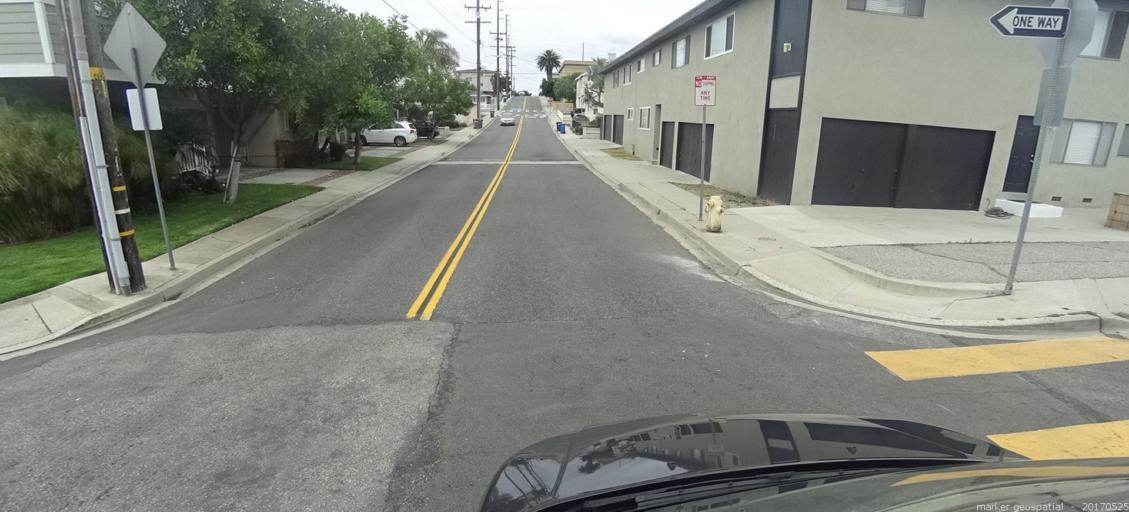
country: US
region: California
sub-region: Los Angeles County
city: Hermosa Beach
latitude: 33.8700
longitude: -118.3791
